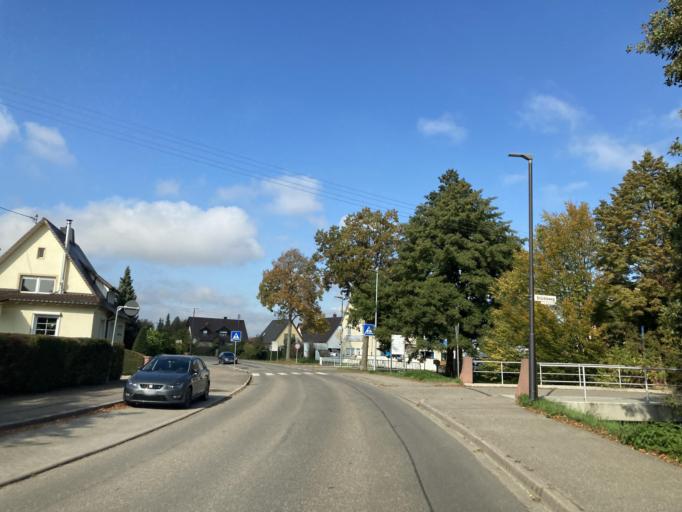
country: DE
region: Baden-Wuerttemberg
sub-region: Freiburg Region
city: Buggingen
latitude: 47.8503
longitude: 7.6376
